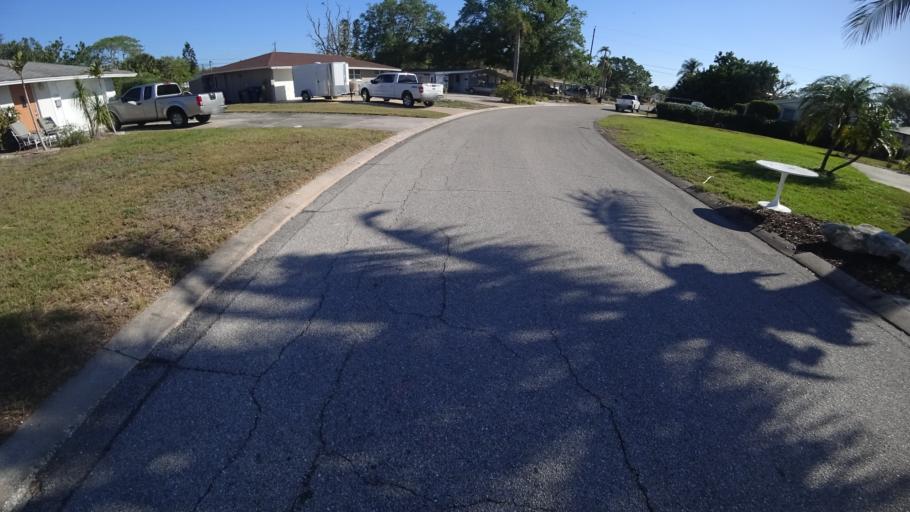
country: US
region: Florida
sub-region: Manatee County
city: Bayshore Gardens
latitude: 27.4229
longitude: -82.5945
